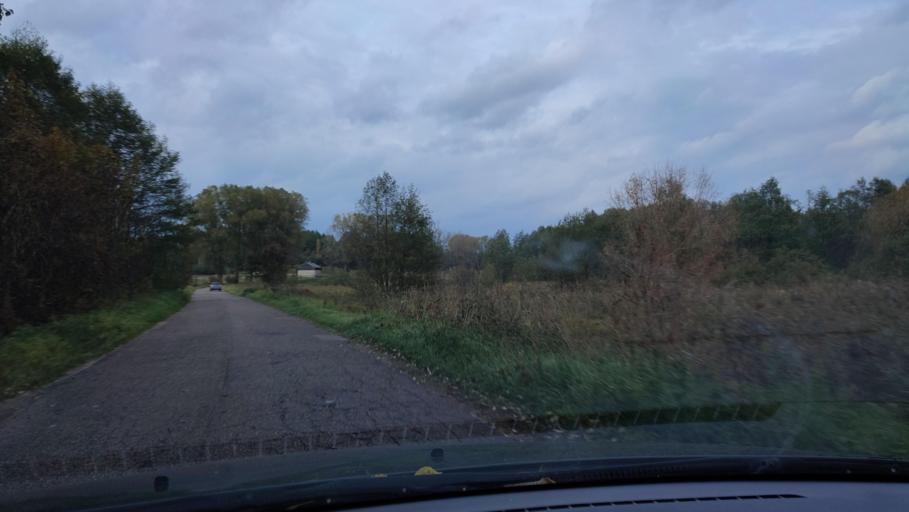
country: PL
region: Masovian Voivodeship
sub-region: Powiat mlawski
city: Mlawa
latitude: 53.1769
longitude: 20.3668
